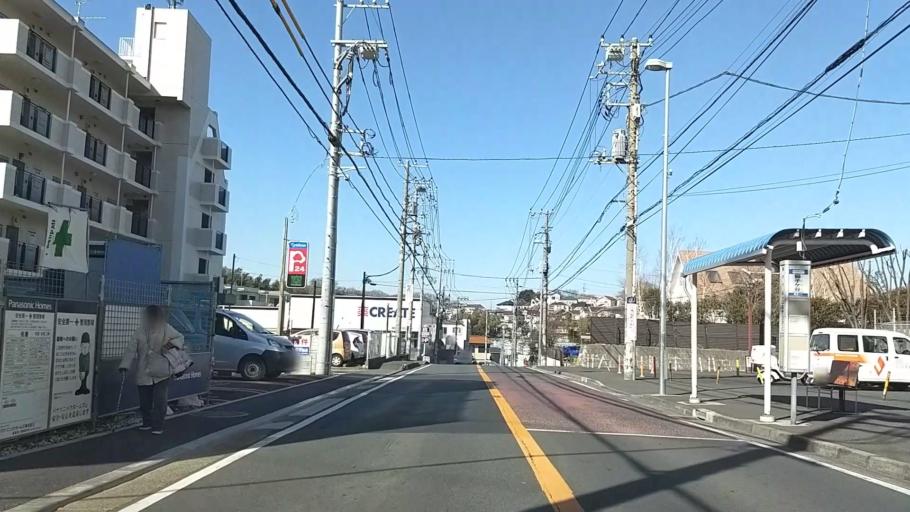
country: JP
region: Kanagawa
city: Yokohama
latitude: 35.5158
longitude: 139.6490
